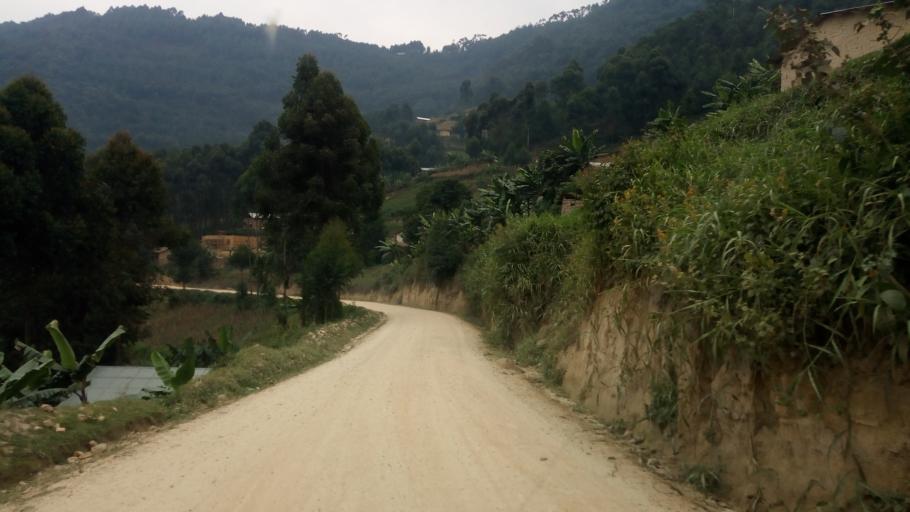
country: UG
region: Western Region
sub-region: Kanungu District
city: Kanungu
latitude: -1.1081
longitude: 29.8641
